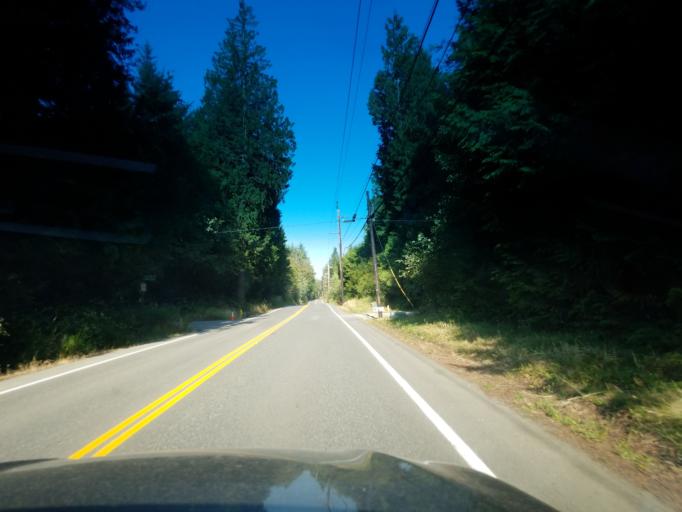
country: US
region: Washington
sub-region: King County
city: Ames Lake
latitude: 47.6571
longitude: -121.9954
